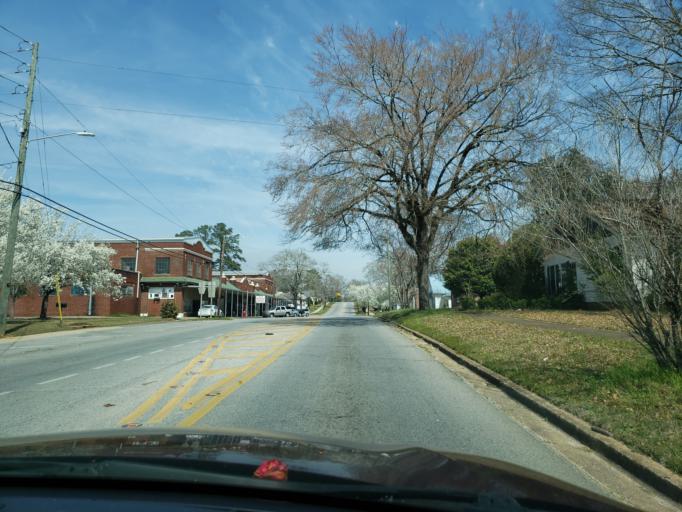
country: US
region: Alabama
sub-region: Elmore County
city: Tallassee
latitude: 32.5343
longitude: -85.8825
